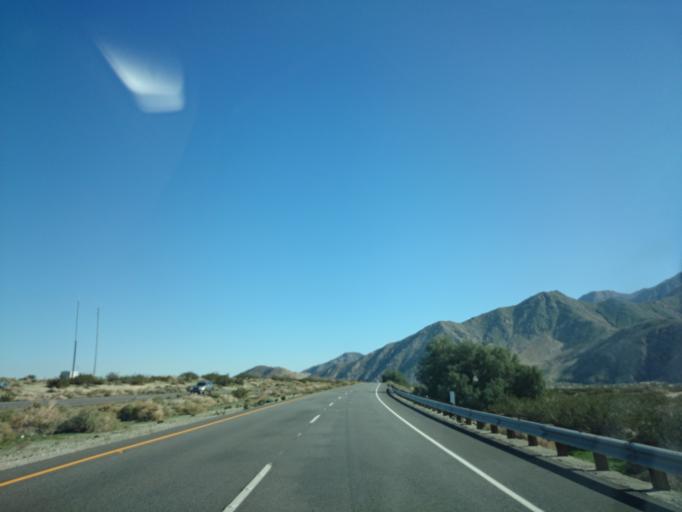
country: US
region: California
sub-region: Riverside County
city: Garnet
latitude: 33.9112
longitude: -116.6580
